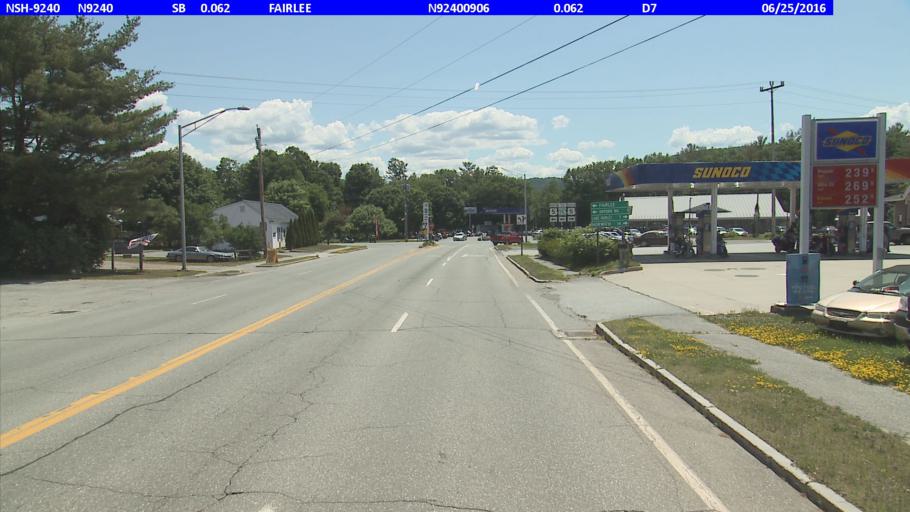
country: US
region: New Hampshire
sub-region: Grafton County
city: Orford
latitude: 43.9047
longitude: -72.1506
